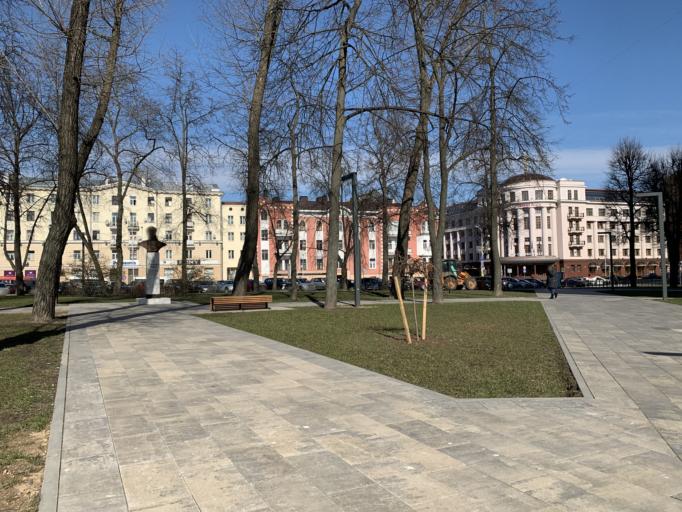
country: BY
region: Minsk
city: Minsk
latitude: 53.8938
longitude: 27.5546
